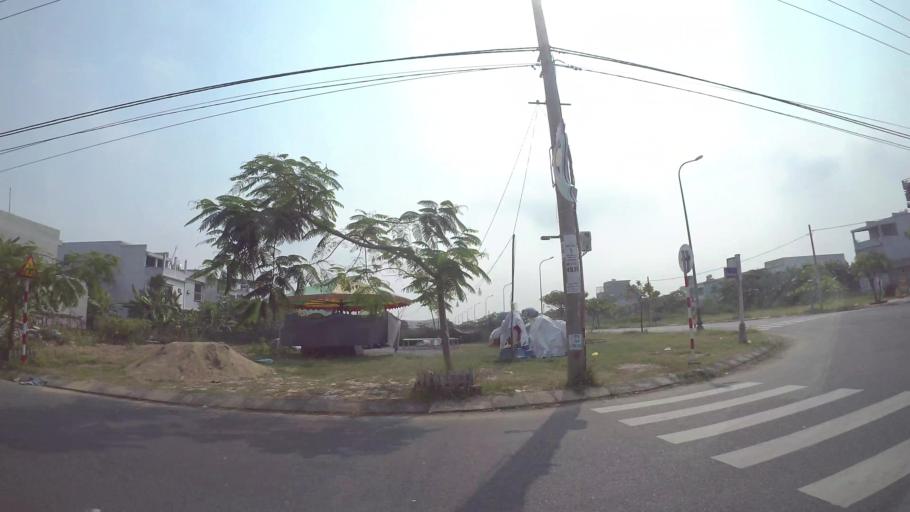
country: VN
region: Da Nang
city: Cam Le
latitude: 15.9948
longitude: 108.2134
